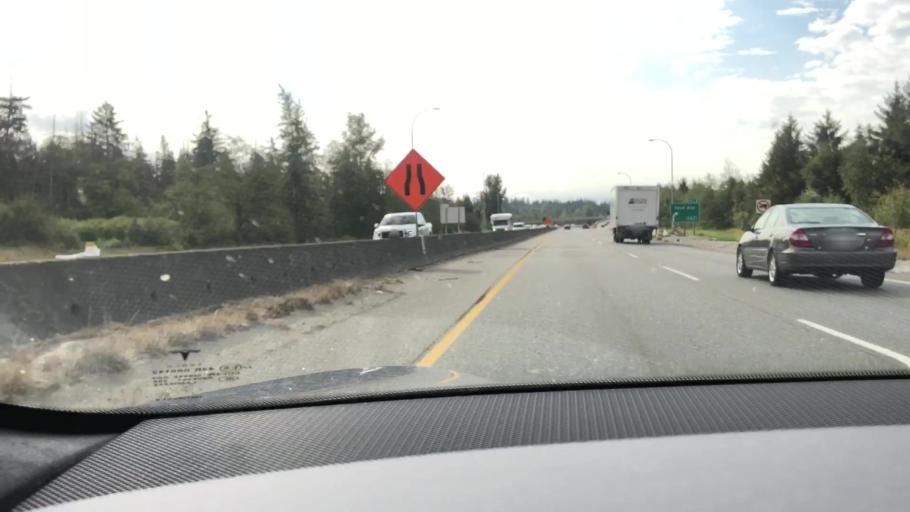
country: CA
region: British Columbia
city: Delta
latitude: 49.1390
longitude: -122.9334
